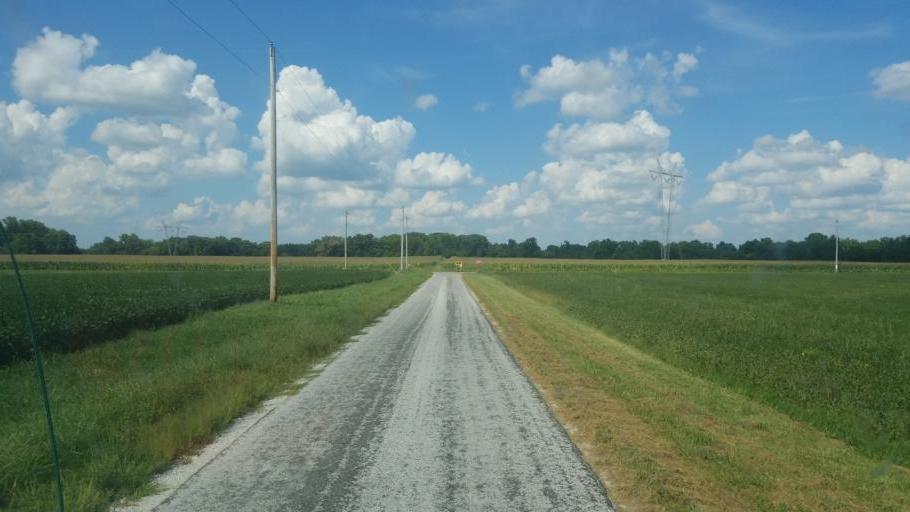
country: US
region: Ohio
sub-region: Wyandot County
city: Carey
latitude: 40.9699
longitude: -83.2471
